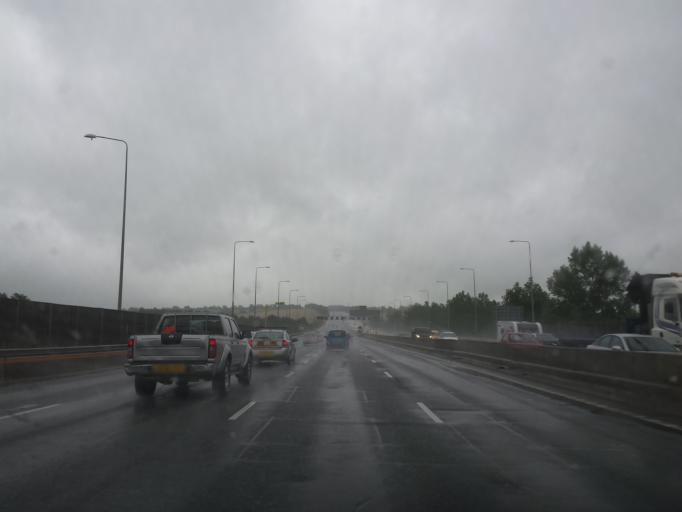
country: GB
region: England
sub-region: Derbyshire
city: Pinxton
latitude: 53.0929
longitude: -1.3081
